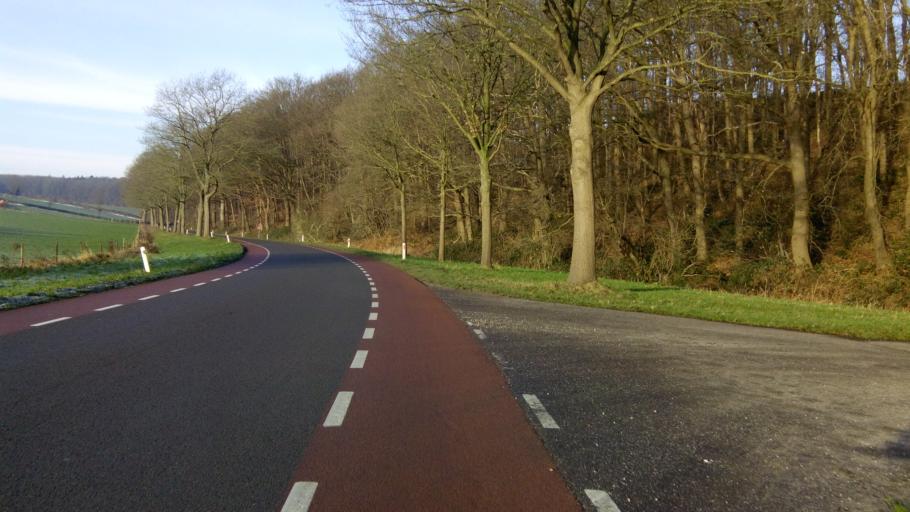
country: NL
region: Gelderland
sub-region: Gemeente Groesbeek
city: De Horst
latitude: 51.8098
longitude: 5.9561
